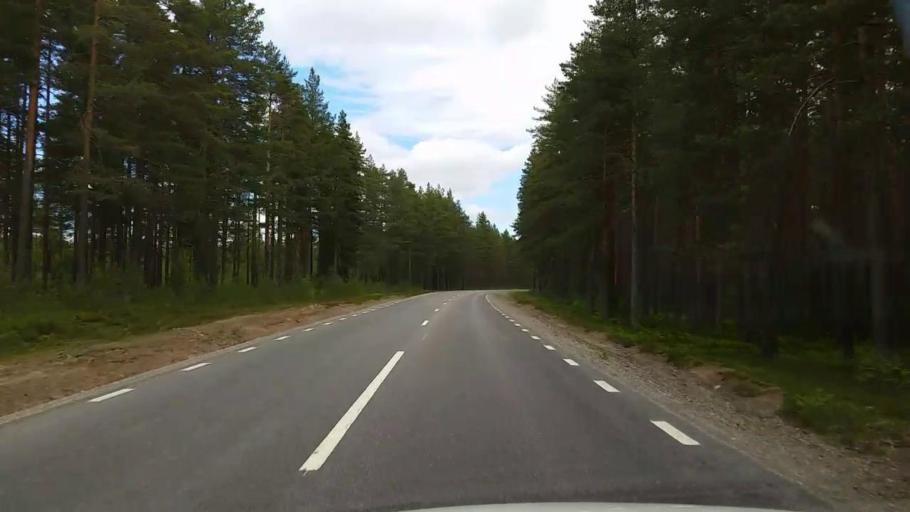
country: SE
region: Gaevleborg
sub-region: Sandvikens Kommun
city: Jarbo
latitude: 60.9490
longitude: 16.3928
